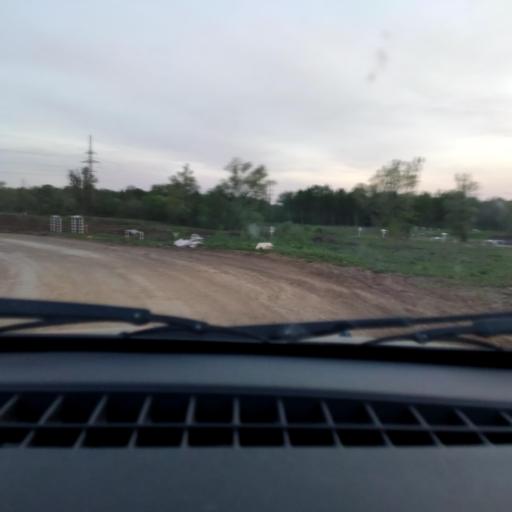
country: RU
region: Bashkortostan
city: Iglino
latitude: 54.8889
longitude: 56.3860
